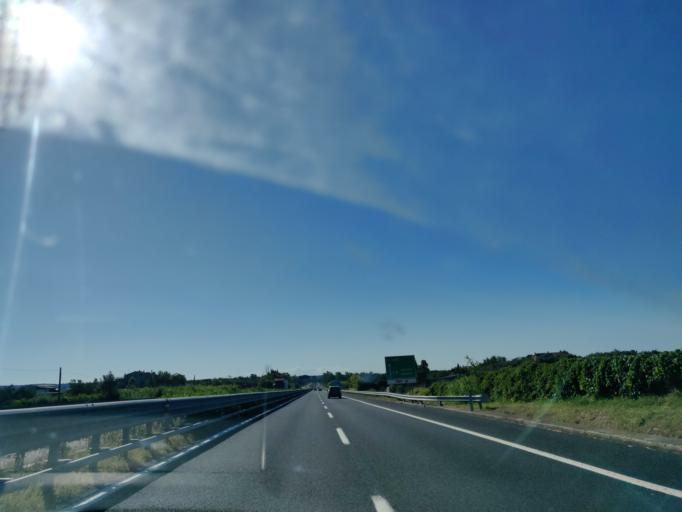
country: IT
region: Latium
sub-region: Citta metropolitana di Roma Capitale
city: Cerveteri
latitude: 41.9850
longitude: 12.0721
